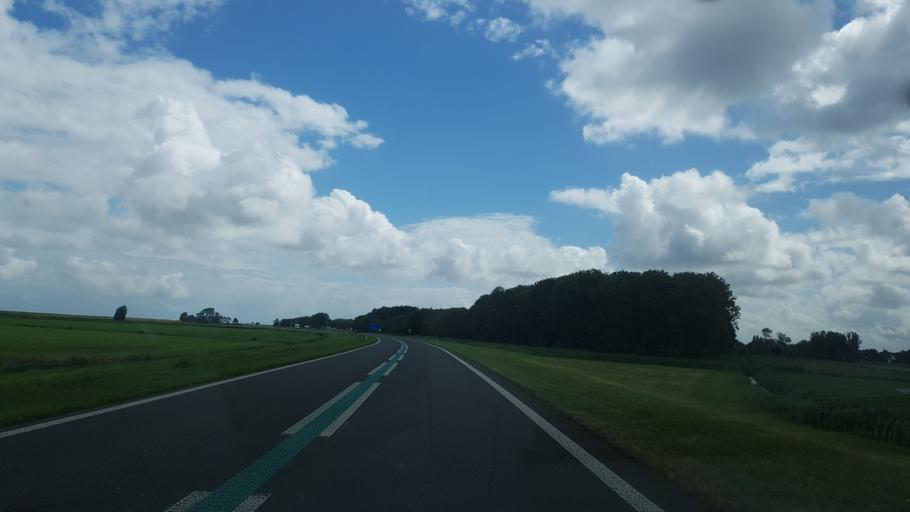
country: NL
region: Friesland
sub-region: Gemeente Dongeradeel
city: Anjum
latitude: 53.3772
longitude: 6.1154
